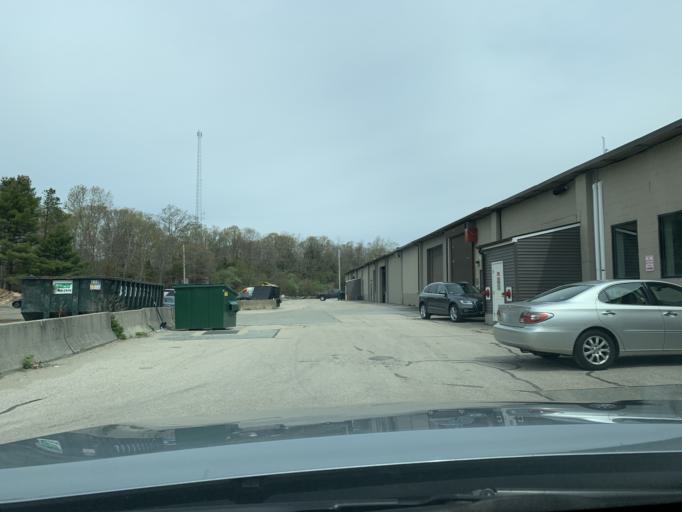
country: US
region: Rhode Island
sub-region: Washington County
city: North Kingstown
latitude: 41.6038
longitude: -71.4784
